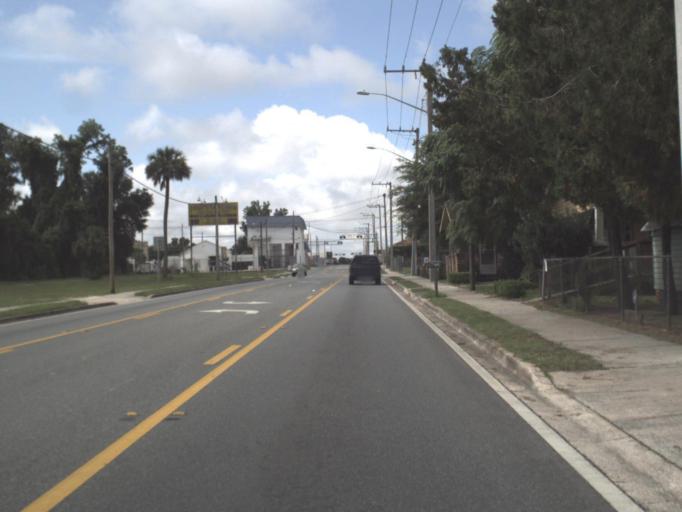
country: US
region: Florida
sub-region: Columbia County
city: Five Points
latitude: 30.2006
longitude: -82.6374
